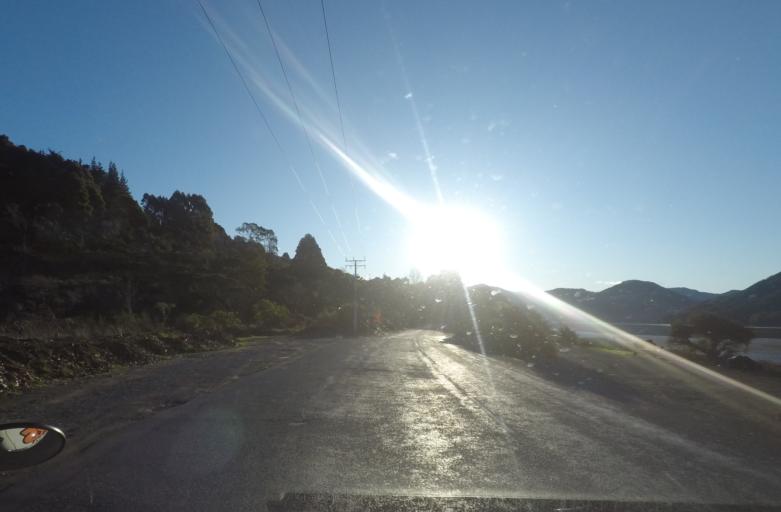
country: NZ
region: Marlborough
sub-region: Marlborough District
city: Picton
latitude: -41.2923
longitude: 173.8204
